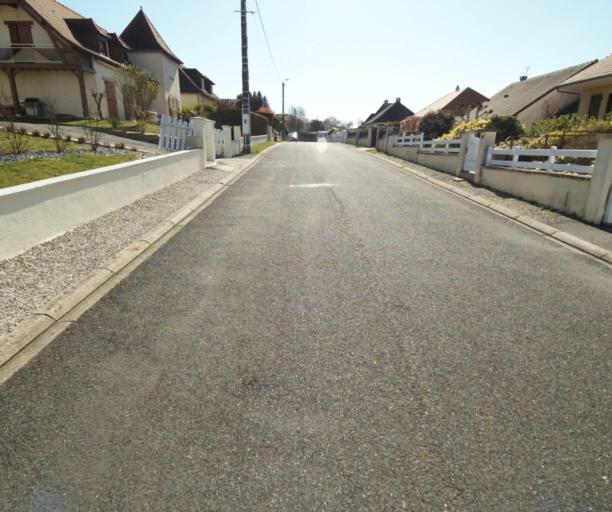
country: FR
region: Limousin
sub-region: Departement de la Correze
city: Seilhac
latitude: 45.3703
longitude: 1.7172
